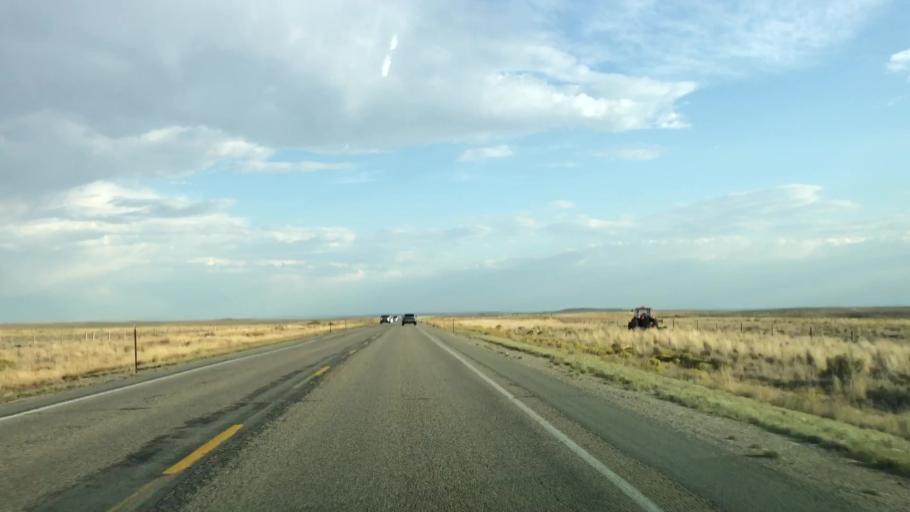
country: US
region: Wyoming
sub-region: Sublette County
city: Pinedale
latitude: 42.4018
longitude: -109.5471
